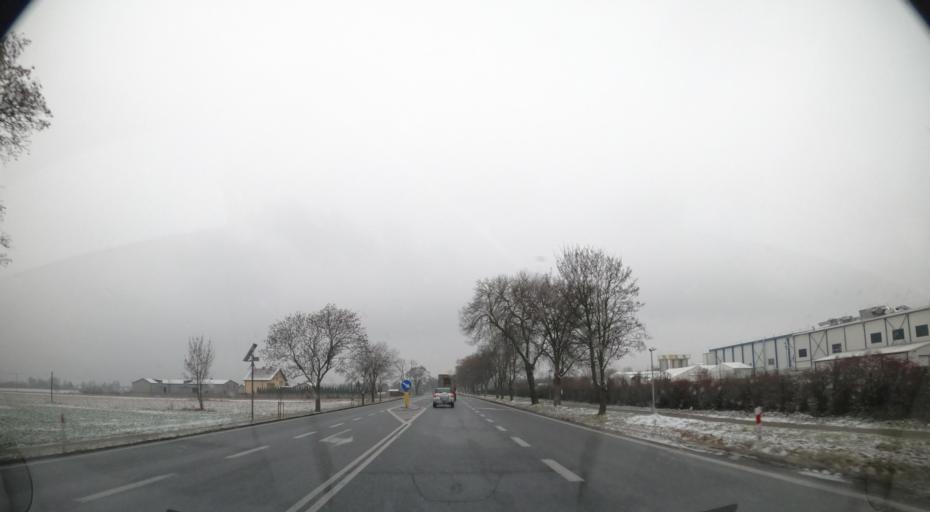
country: PL
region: Masovian Voivodeship
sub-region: Powiat sochaczewski
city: Teresin
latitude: 52.2210
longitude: 20.3306
